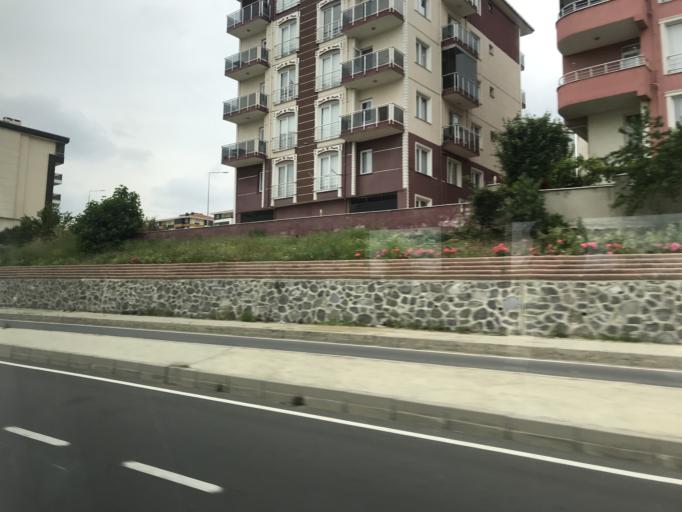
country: TR
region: Tekirdag
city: Malkara
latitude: 40.8861
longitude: 26.8996
